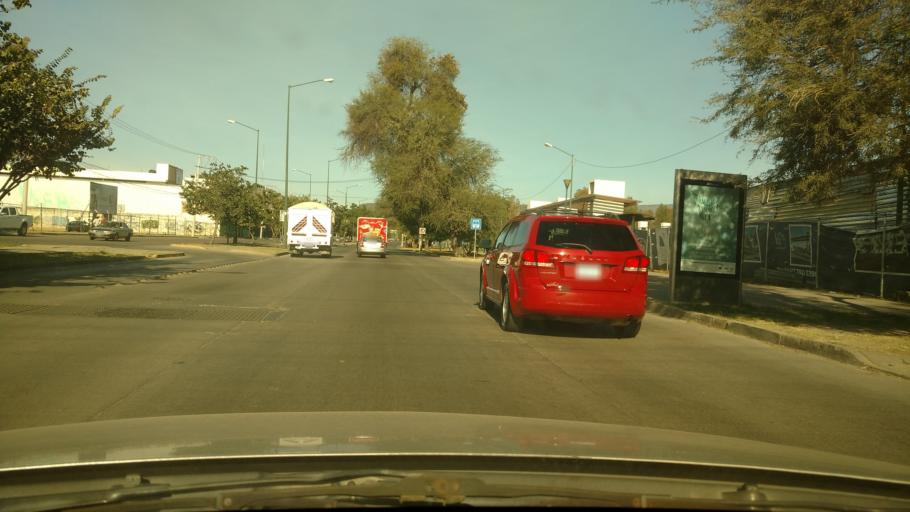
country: MX
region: Guanajuato
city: Leon
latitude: 21.1672
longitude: -101.6613
